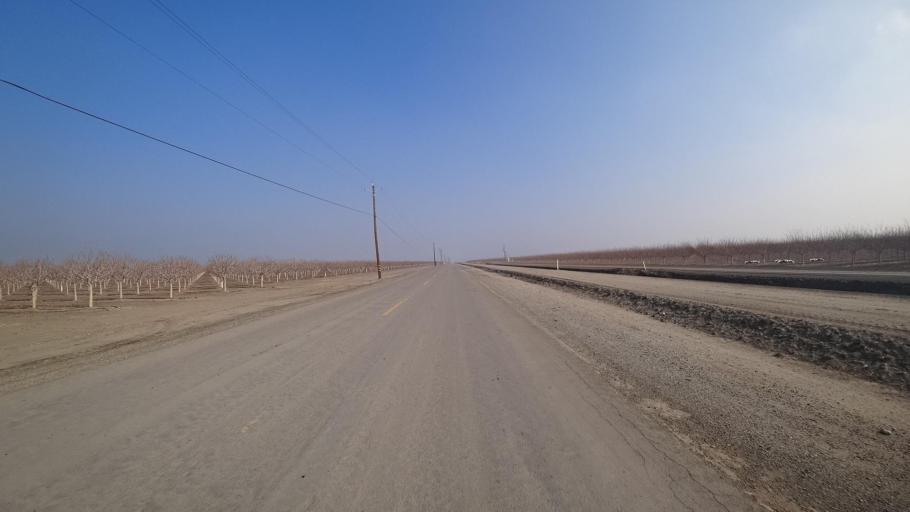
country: US
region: California
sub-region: Kern County
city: Greenfield
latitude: 35.1514
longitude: -119.0685
